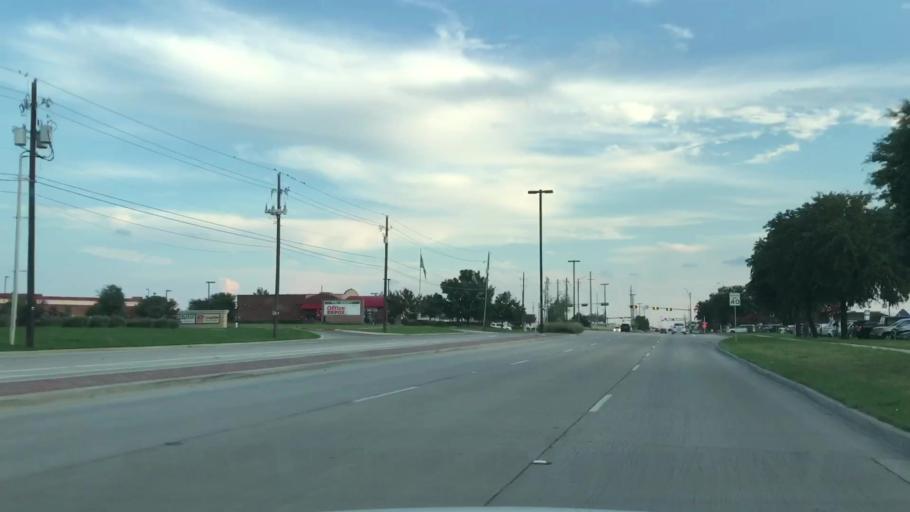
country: US
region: Texas
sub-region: Dallas County
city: Carrollton
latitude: 32.9877
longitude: -96.9100
